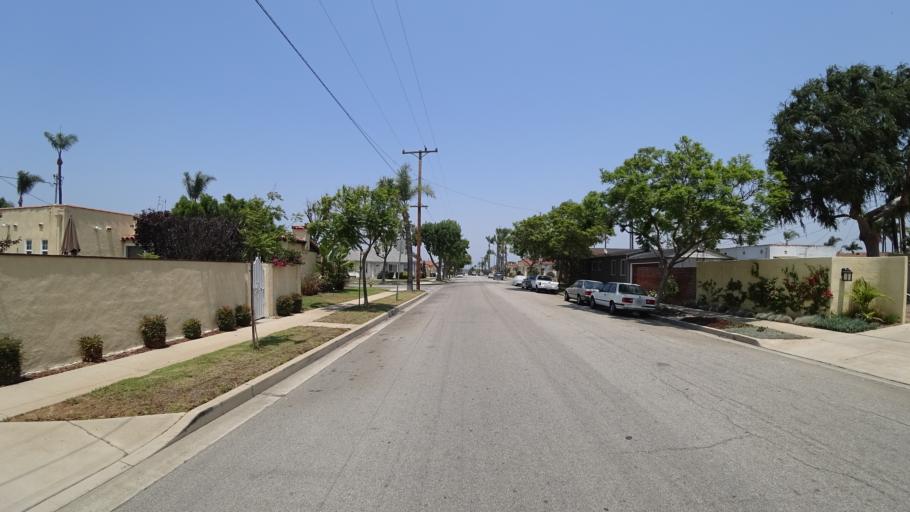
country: US
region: California
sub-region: Los Angeles County
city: Inglewood
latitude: 33.9667
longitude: -118.3330
